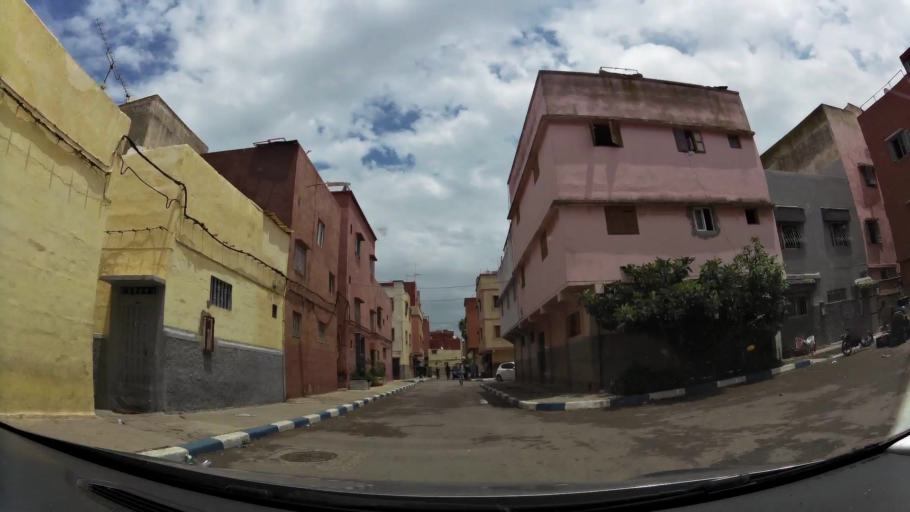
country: MA
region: Rabat-Sale-Zemmour-Zaer
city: Sale
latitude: 34.0401
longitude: -6.8121
